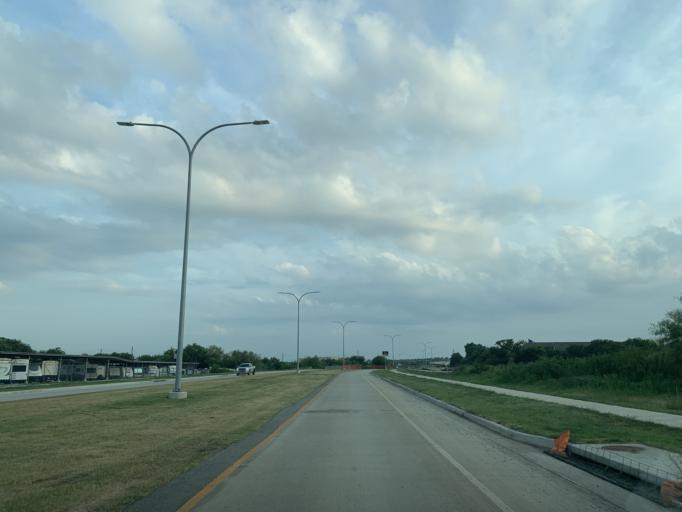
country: US
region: Texas
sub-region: Tarrant County
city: Keller
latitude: 32.9361
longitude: -97.2718
